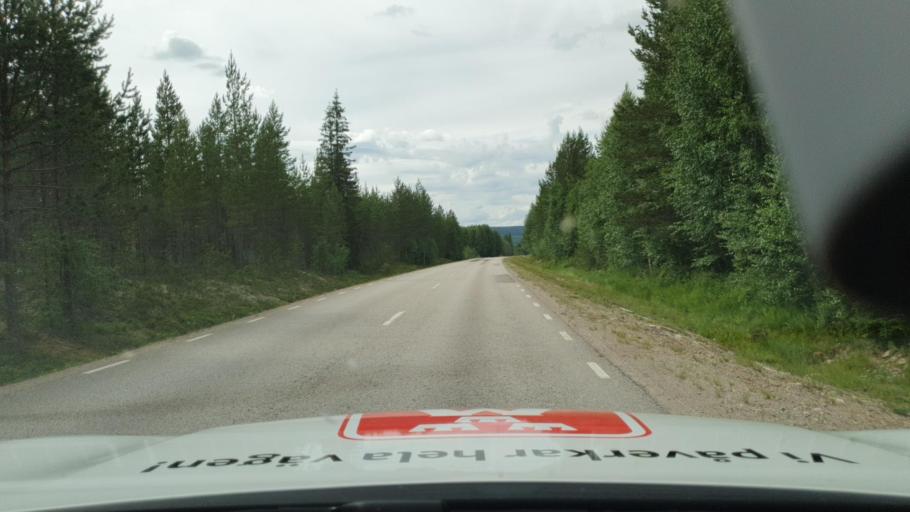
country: NO
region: Hedmark
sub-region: Trysil
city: Innbygda
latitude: 60.9313
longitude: 12.4979
